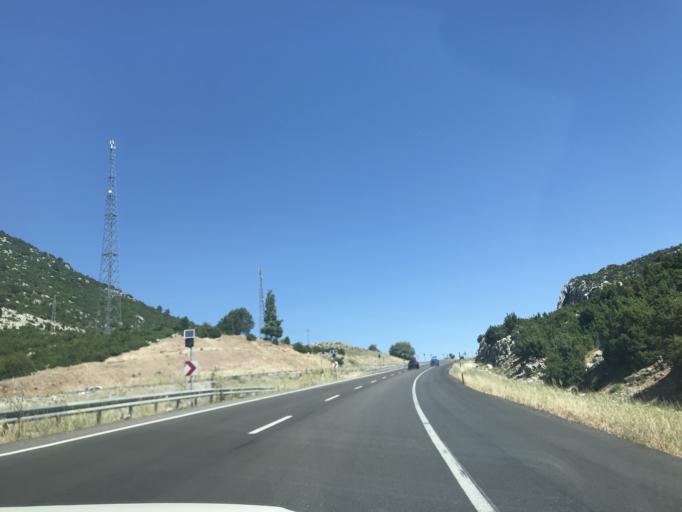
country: TR
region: Antalya
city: Dagbeli
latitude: 37.1660
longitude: 30.4997
